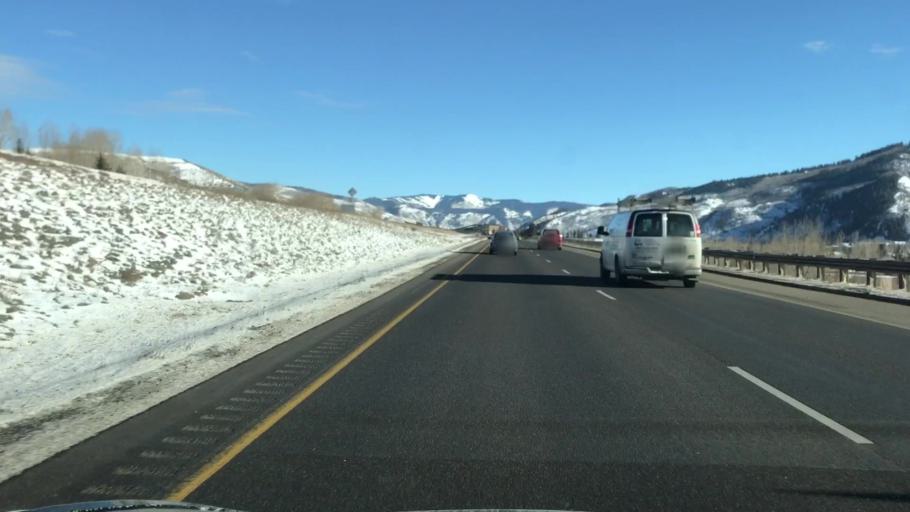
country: US
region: Colorado
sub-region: Eagle County
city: Edwards
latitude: 39.6440
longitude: -106.5775
